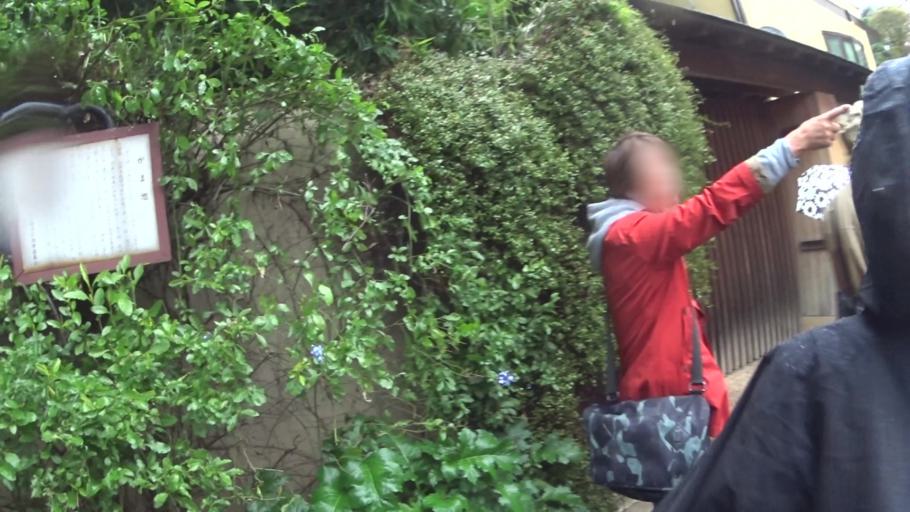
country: JP
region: Tokyo
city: Tokyo
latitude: 35.6538
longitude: 139.7294
